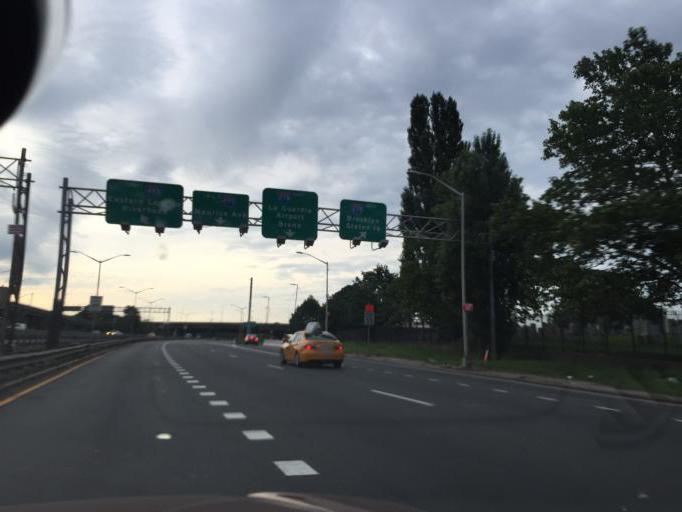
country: US
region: New York
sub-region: Queens County
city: Long Island City
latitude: 40.7358
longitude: -73.9259
